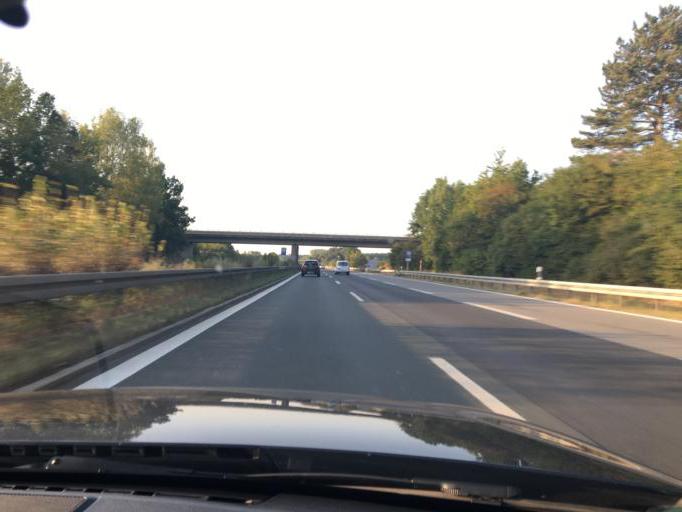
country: DE
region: Bavaria
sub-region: Upper Franconia
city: Hirschaid
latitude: 49.8231
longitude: 11.0094
